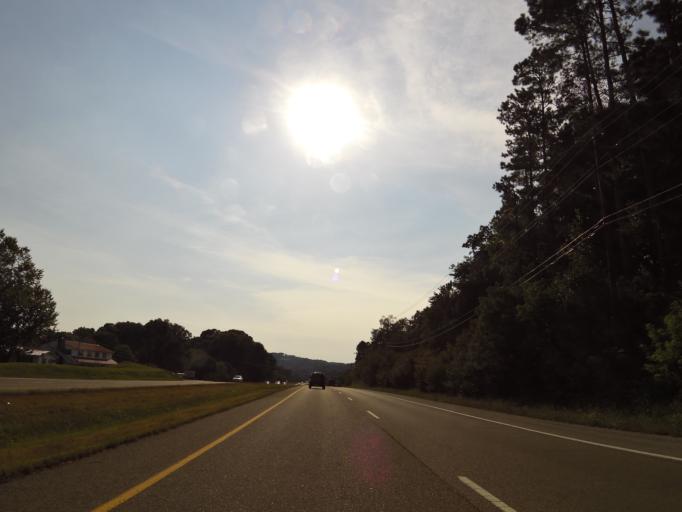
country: US
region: Tennessee
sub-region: Loudon County
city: Lenoir City
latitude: 35.8416
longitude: -84.3023
